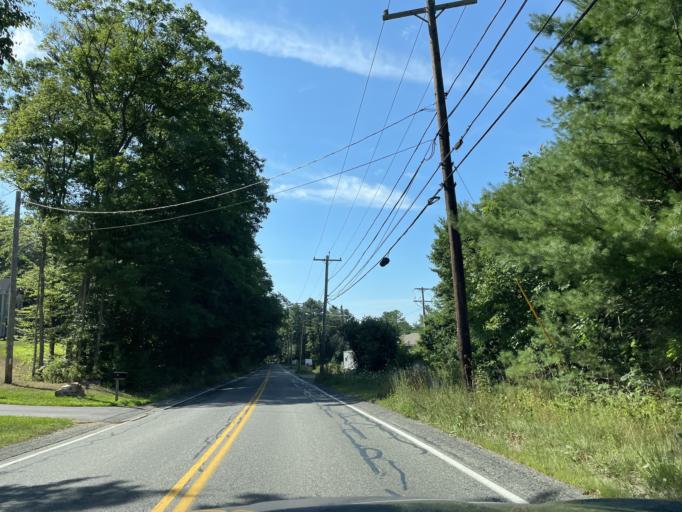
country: US
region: Massachusetts
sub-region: Worcester County
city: Mendon
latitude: 42.1179
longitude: -71.5850
